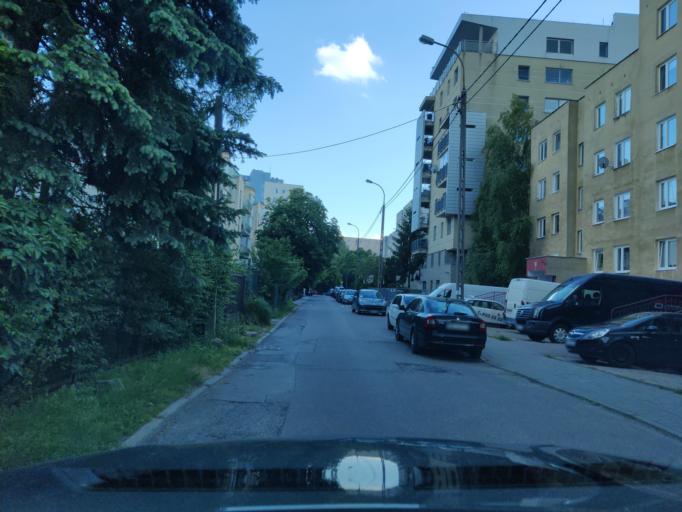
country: PL
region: Masovian Voivodeship
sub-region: Warszawa
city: Mokotow
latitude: 52.1747
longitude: 21.0304
